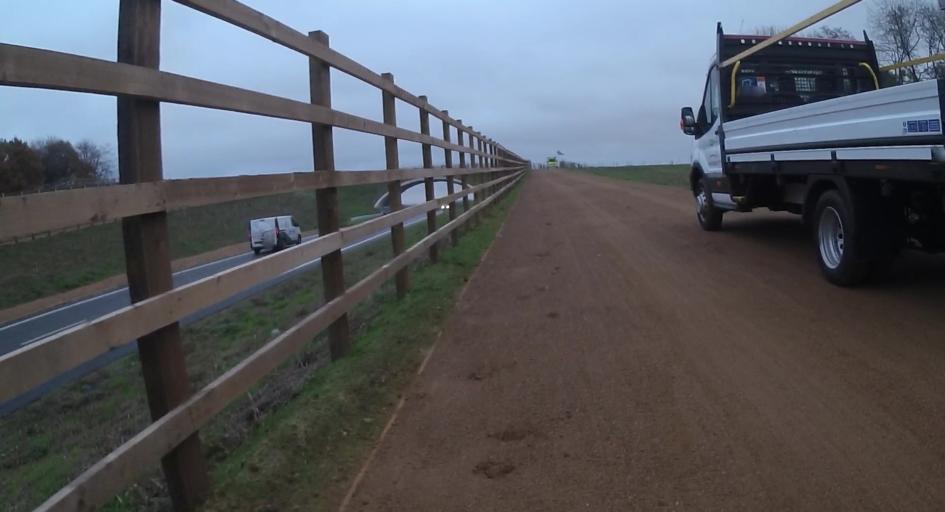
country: GB
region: England
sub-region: West Berkshire
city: Arborfield
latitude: 51.3908
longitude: -0.9129
